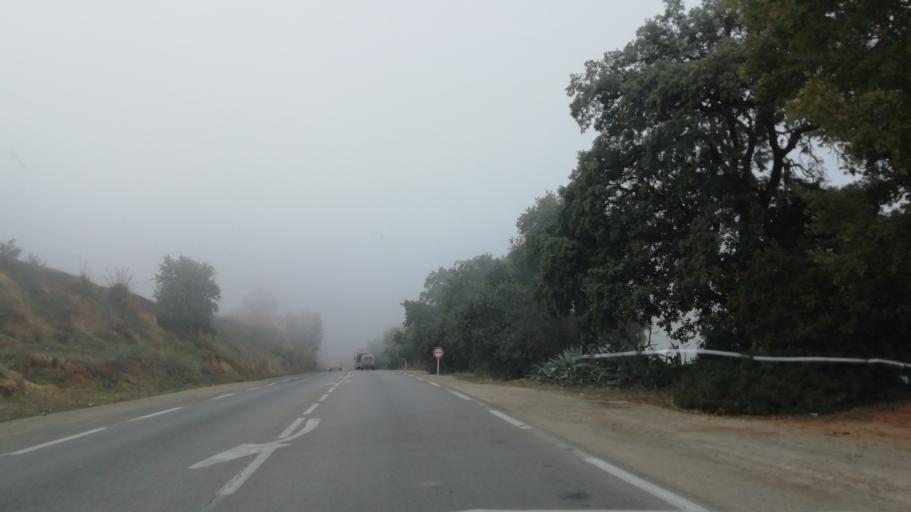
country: DZ
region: Mascara
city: Mascara
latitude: 35.5273
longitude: 0.3364
